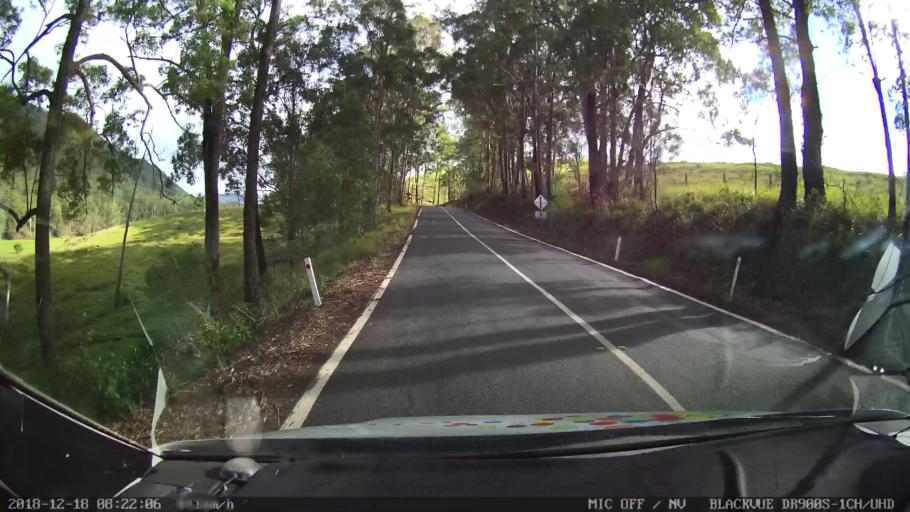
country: AU
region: New South Wales
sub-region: Kyogle
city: Kyogle
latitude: -28.3273
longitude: 152.7246
